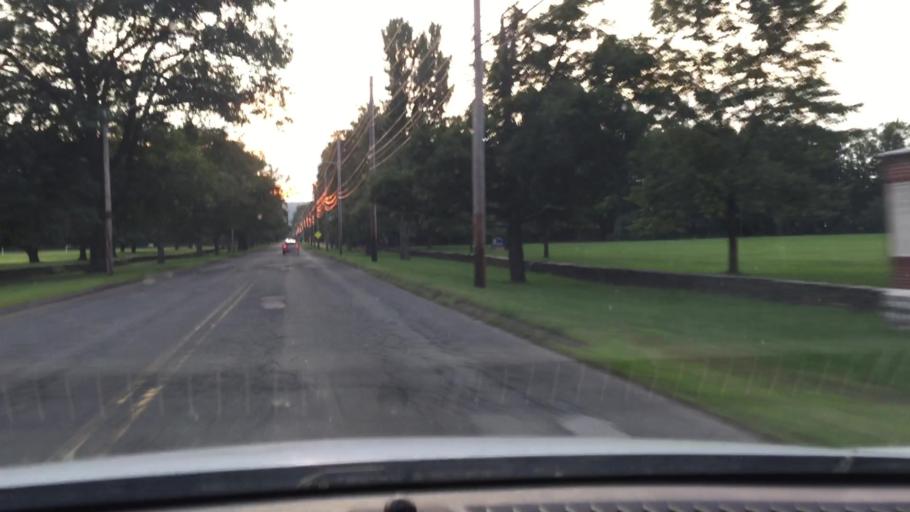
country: US
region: Massachusetts
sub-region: Hampden County
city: Westfield
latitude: 42.1260
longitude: -72.7845
